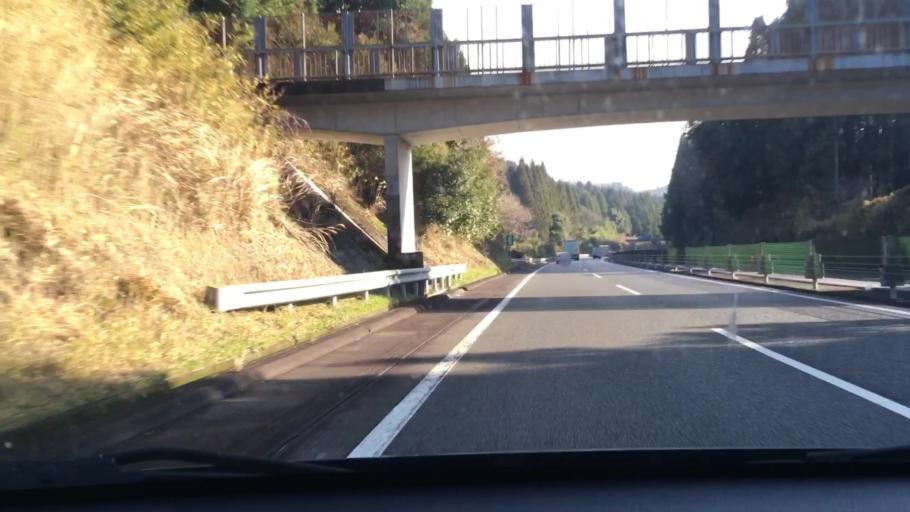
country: JP
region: Kagoshima
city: Okuchi-shinohara
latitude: 32.0015
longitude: 130.7574
